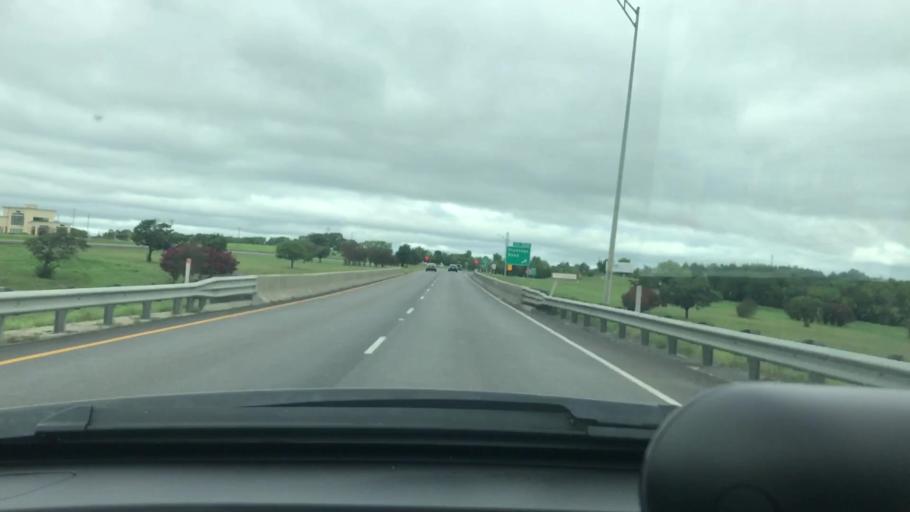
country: US
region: Texas
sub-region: Grayson County
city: Sherman
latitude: 33.6004
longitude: -96.6070
